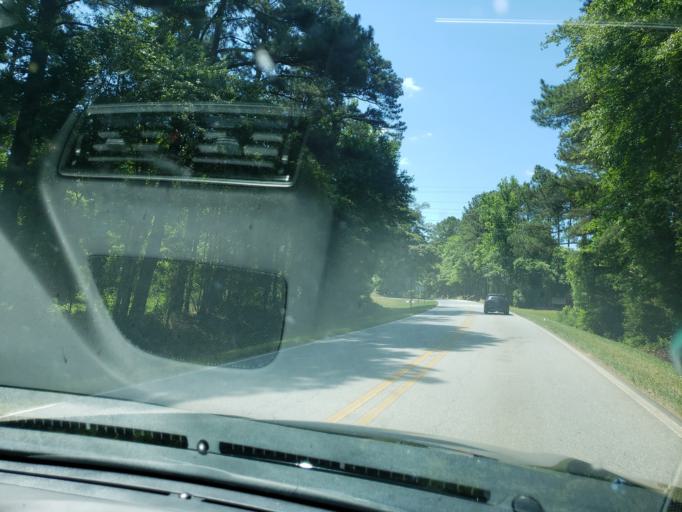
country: US
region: Alabama
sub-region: Lee County
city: Auburn
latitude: 32.6631
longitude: -85.4904
